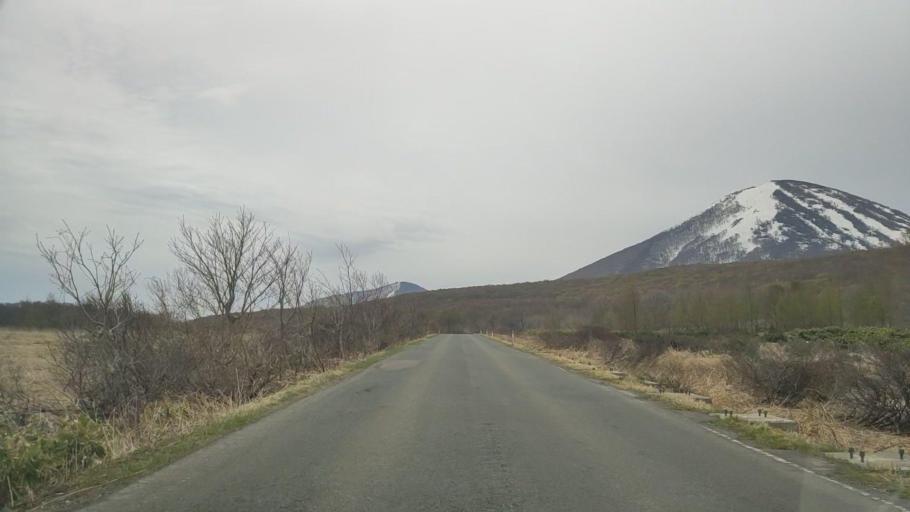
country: JP
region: Aomori
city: Aomori Shi
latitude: 40.6875
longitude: 140.9248
